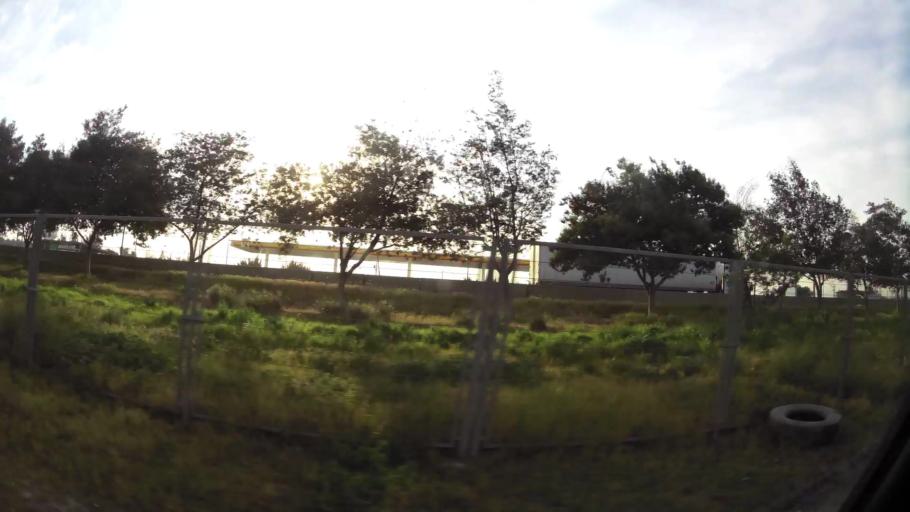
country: CL
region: Santiago Metropolitan
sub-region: Provincia de Maipo
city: San Bernardo
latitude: -33.5268
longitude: -70.7062
